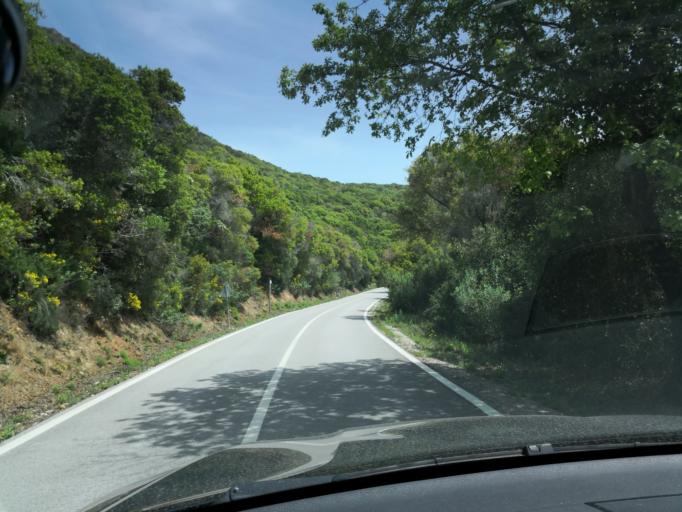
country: PT
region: Setubal
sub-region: Sesimbra
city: Sesimbra
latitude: 38.4710
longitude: -9.0014
